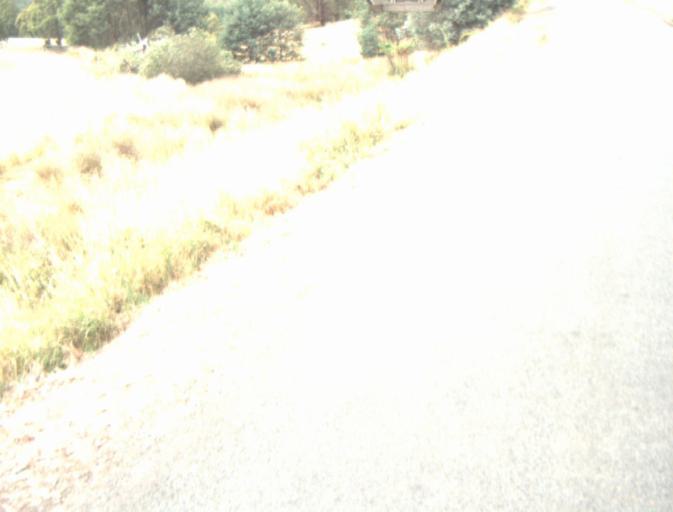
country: AU
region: Tasmania
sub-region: Dorset
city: Scottsdale
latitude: -41.4612
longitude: 147.5954
